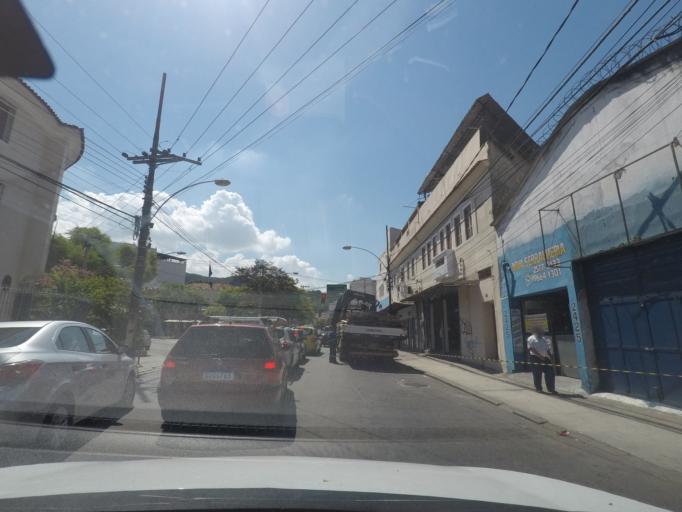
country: BR
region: Rio de Janeiro
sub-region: Rio De Janeiro
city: Rio de Janeiro
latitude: -22.9205
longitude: -43.2594
